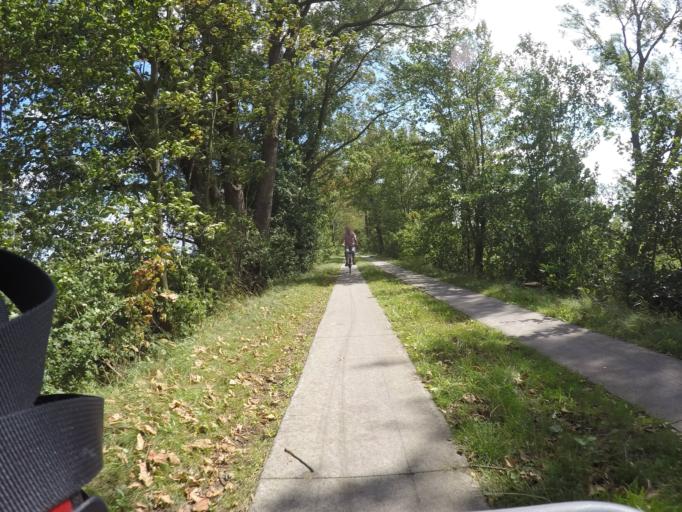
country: DE
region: Lower Saxony
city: Stelle
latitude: 53.4268
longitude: 10.1580
